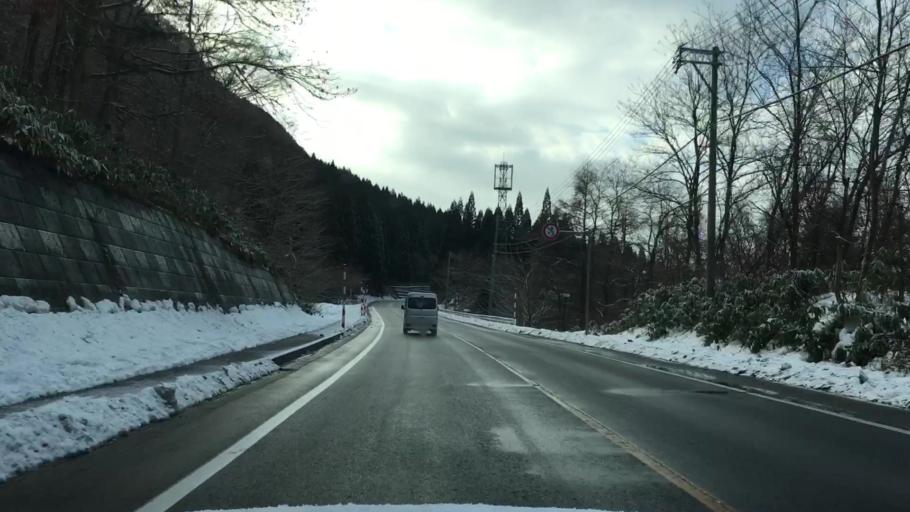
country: JP
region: Akita
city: Odate
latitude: 40.3910
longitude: 140.6049
